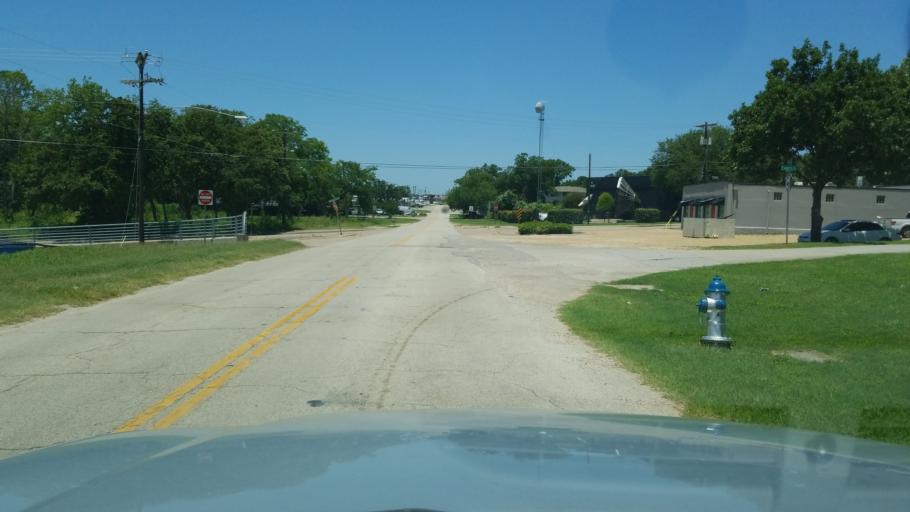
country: US
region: Texas
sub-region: Dallas County
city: Irving
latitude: 32.8034
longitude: -96.9164
